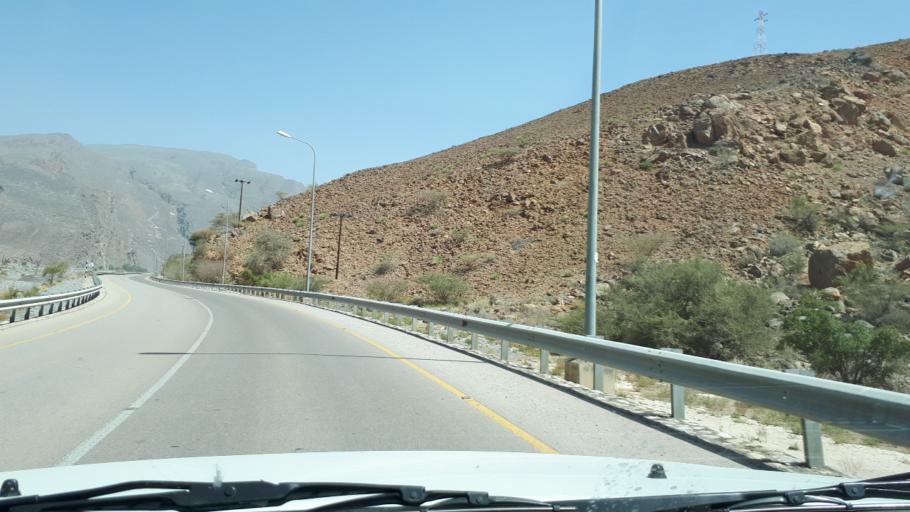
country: OM
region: Muhafazat ad Dakhiliyah
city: Izki
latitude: 22.9429
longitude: 57.6735
